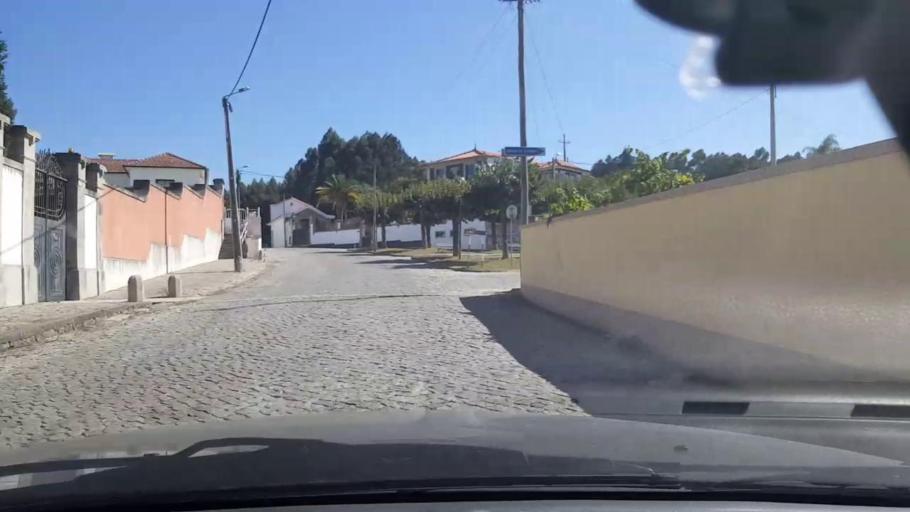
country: PT
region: Porto
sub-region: Maia
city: Gemunde
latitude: 41.3162
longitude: -8.6435
